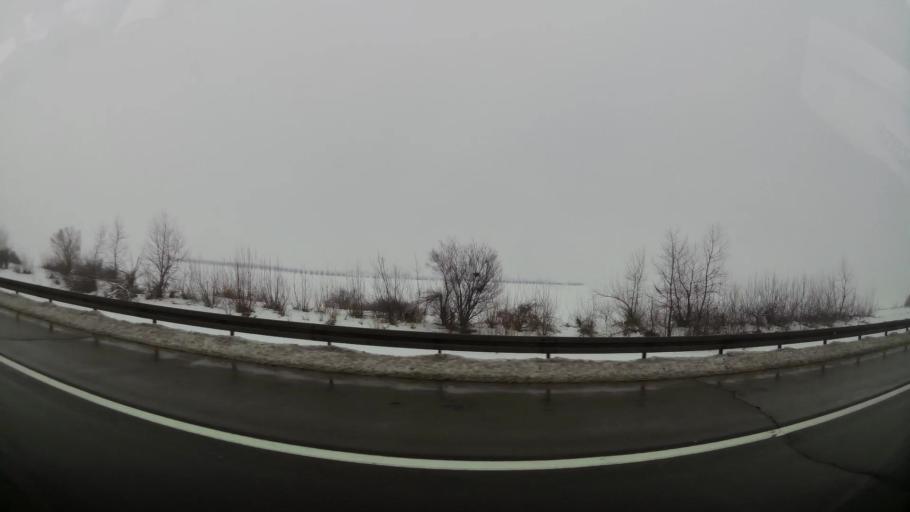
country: RS
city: Dobanovci
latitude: 44.8279
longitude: 20.2518
